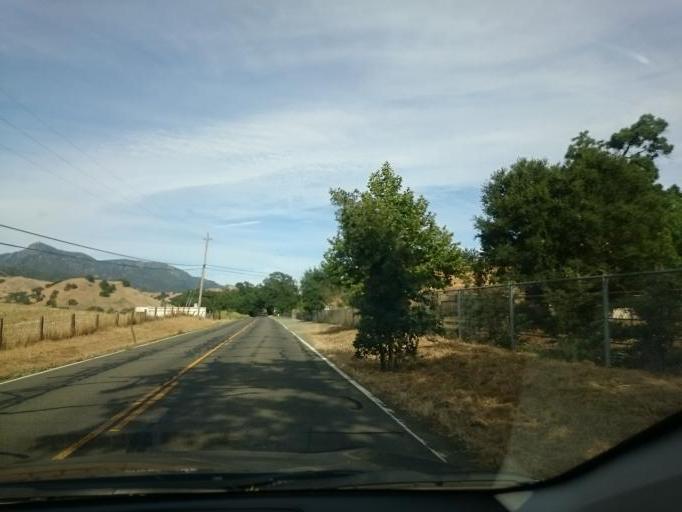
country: US
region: California
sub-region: Sonoma County
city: Windsor
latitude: 38.6489
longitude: -122.7240
